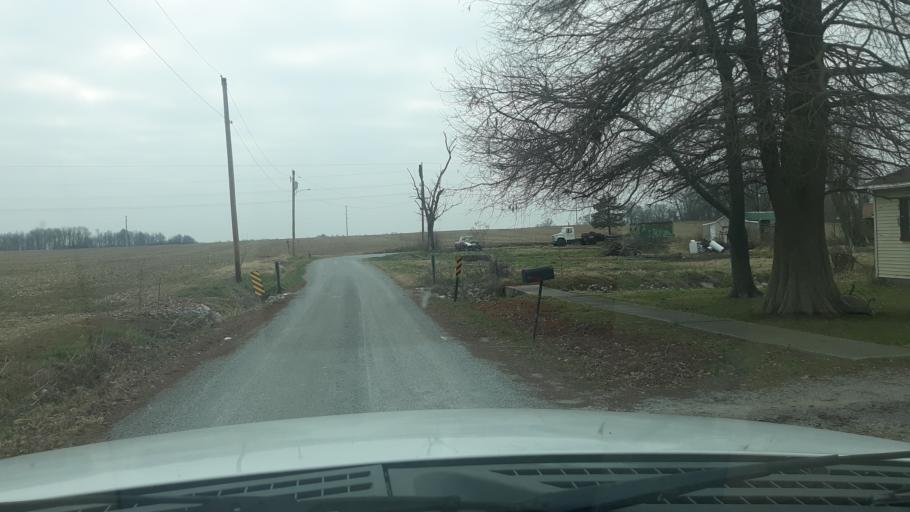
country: US
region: Illinois
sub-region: Saline County
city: Harrisburg
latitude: 37.8350
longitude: -88.6121
